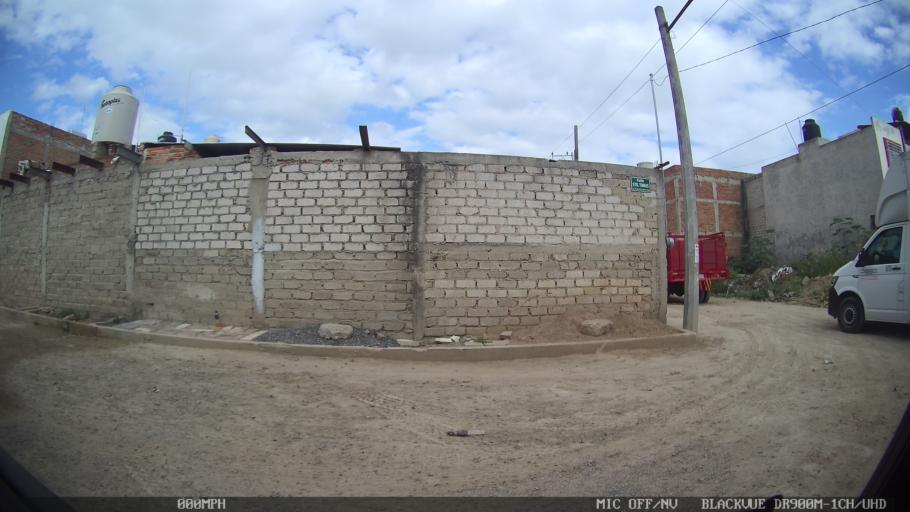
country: MX
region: Jalisco
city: Tonala
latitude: 20.6562
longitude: -103.2370
